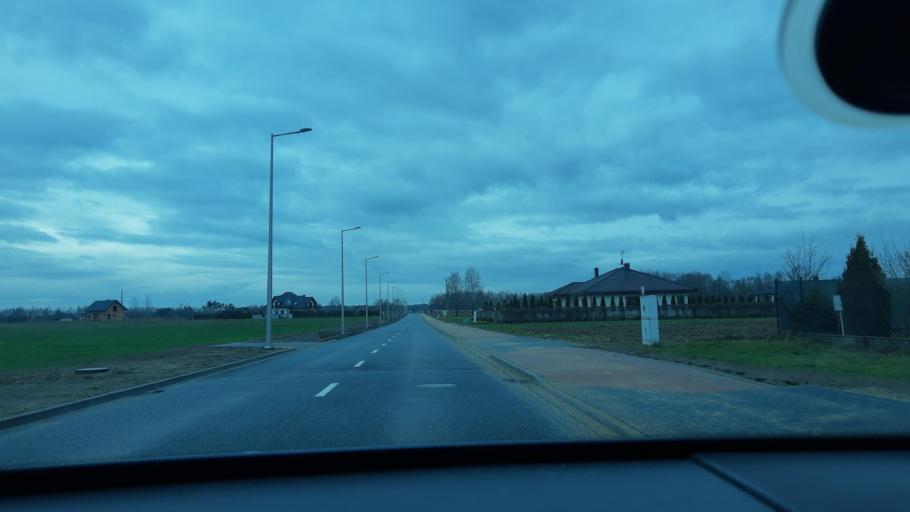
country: PL
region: Lodz Voivodeship
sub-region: Powiat sieradzki
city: Sieradz
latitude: 51.5849
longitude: 18.6839
